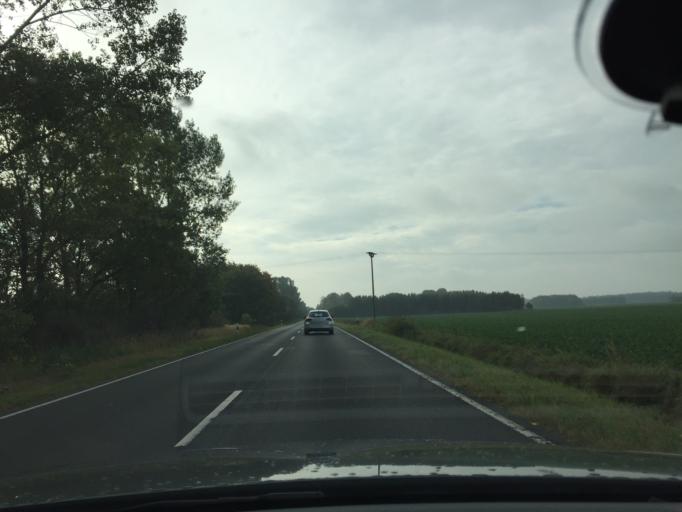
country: DE
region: Mecklenburg-Vorpommern
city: Ostseebad Dierhagen
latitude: 54.2377
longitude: 12.3627
